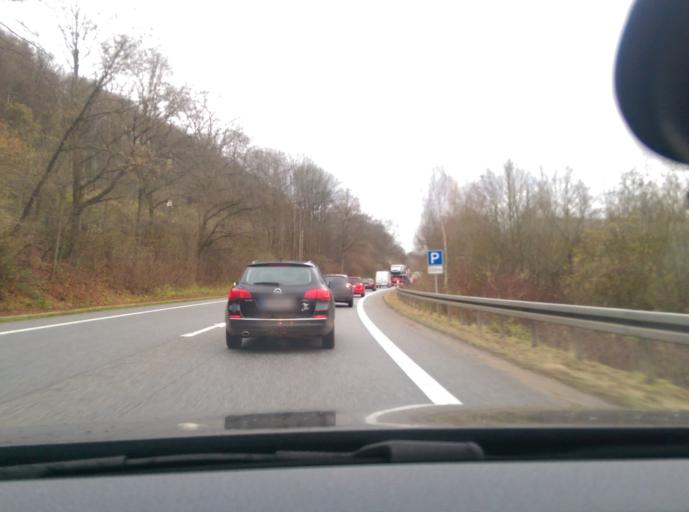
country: DE
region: Thuringia
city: Lindewerra
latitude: 51.3020
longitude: 9.9448
